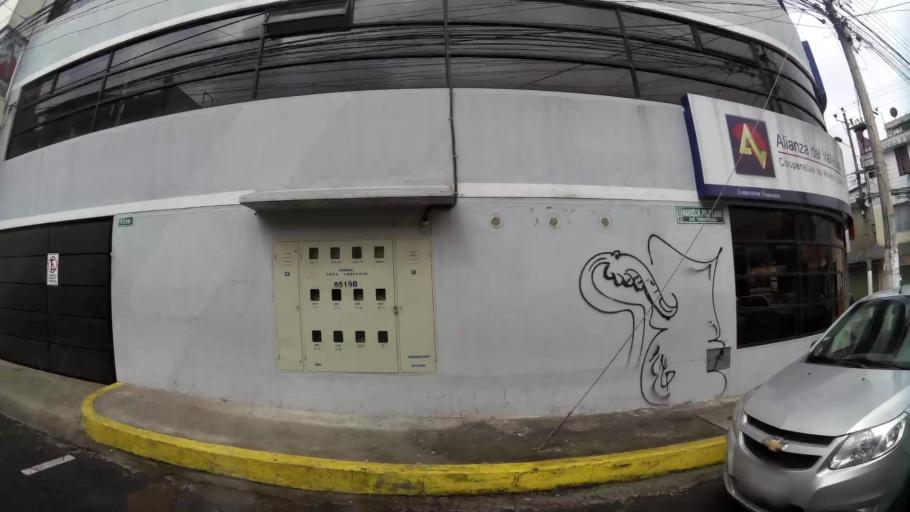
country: EC
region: Pichincha
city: Sangolqui
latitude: -0.2935
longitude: -78.4771
